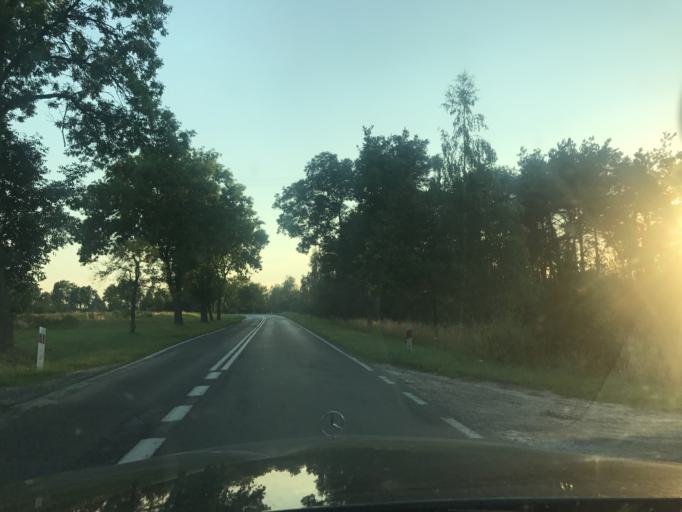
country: PL
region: Lublin Voivodeship
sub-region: Powiat lubartowski
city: Lubartow
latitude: 51.4977
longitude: 22.6413
